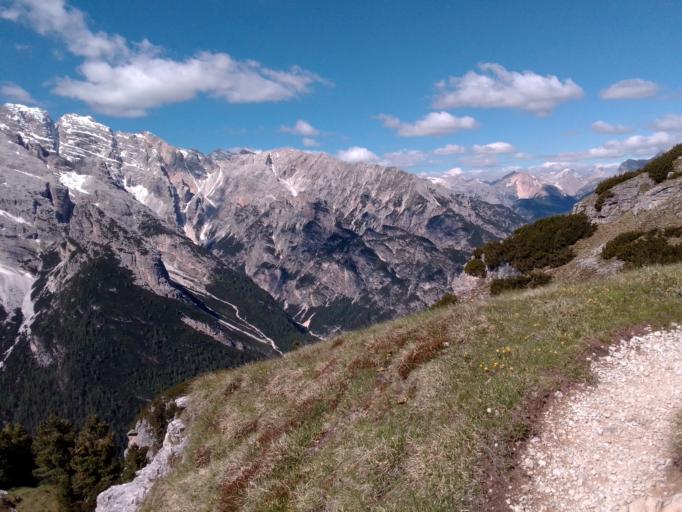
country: IT
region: Trentino-Alto Adige
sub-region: Bolzano
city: Dobbiaco
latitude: 46.6132
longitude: 12.2473
